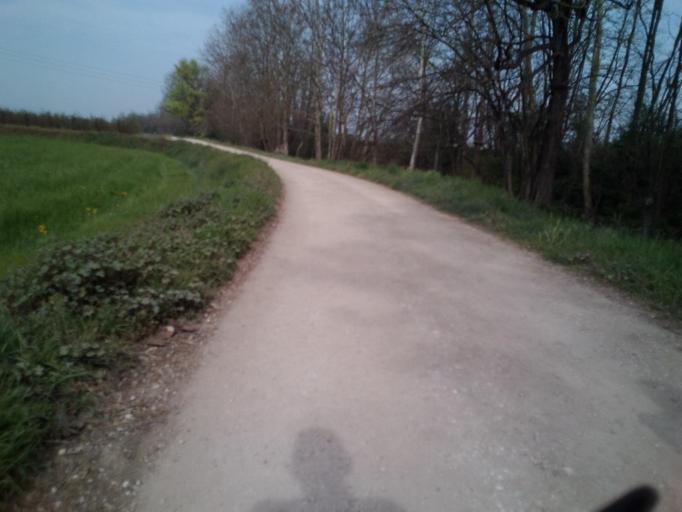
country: IT
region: Veneto
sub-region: Provincia di Verona
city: Rosegaferro
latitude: 45.3589
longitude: 10.8026
